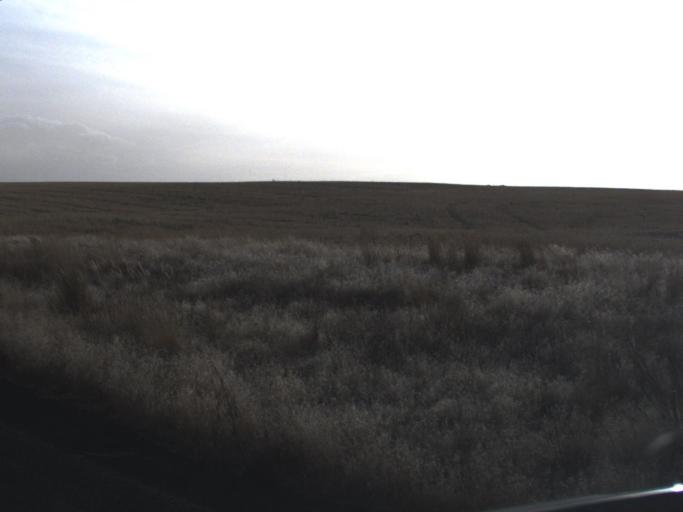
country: US
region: Washington
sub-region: Adams County
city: Ritzville
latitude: 47.2752
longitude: -118.6909
